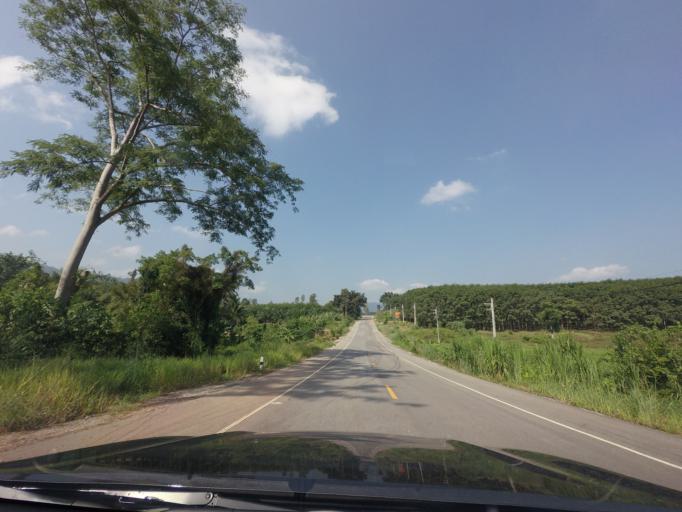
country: TH
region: Loei
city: Na Haeo
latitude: 17.4975
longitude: 101.0392
